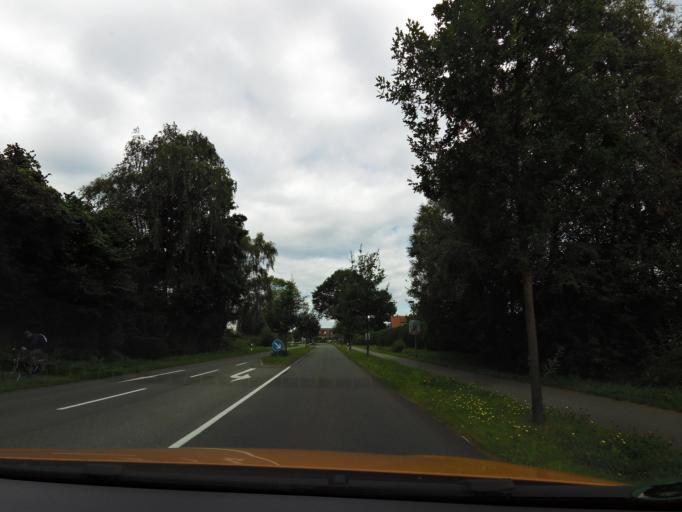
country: DE
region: Lower Saxony
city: Oldenburg
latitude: 53.1672
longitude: 8.1544
